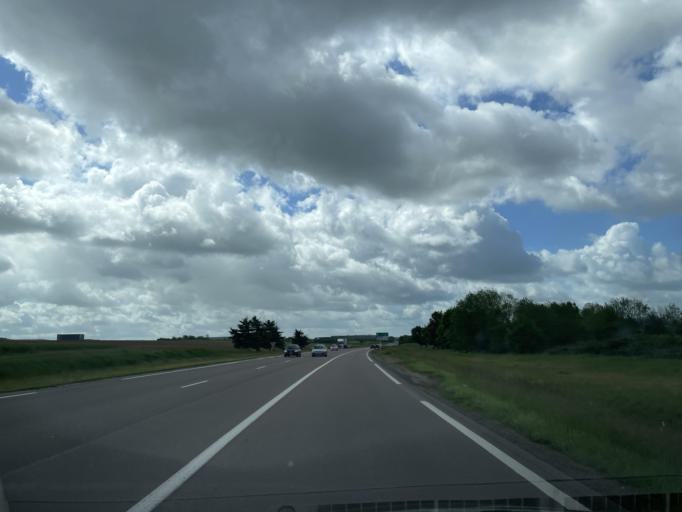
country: FR
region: Bourgogne
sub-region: Departement de l'Yonne
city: Saint-Clement
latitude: 48.2115
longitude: 3.3100
